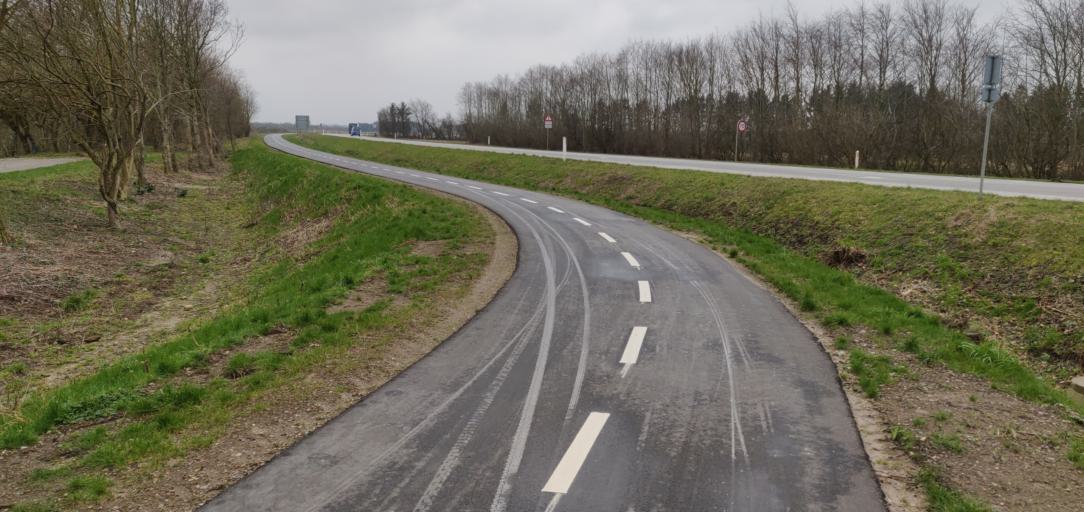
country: DK
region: South Denmark
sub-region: Haderslev Kommune
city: Vojens
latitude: 55.2367
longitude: 9.2962
